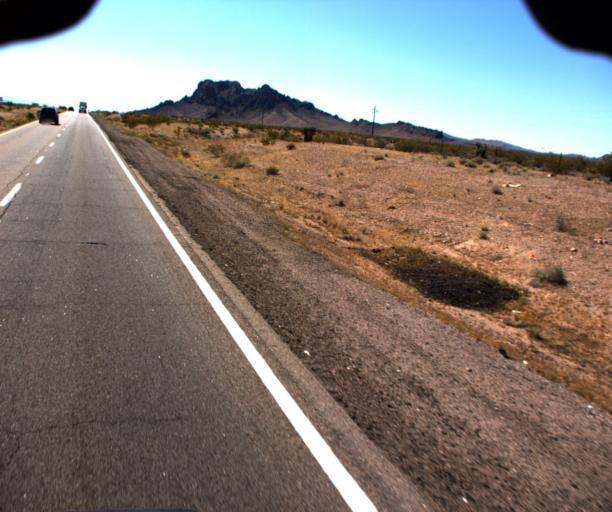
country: US
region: Nevada
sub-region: Clark County
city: Boulder City
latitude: 35.8116
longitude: -114.5453
